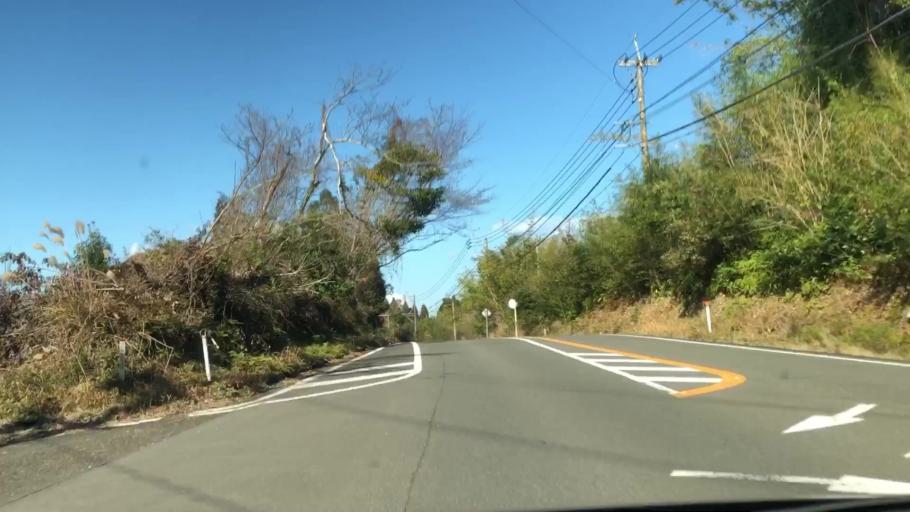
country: JP
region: Kagoshima
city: Satsumasendai
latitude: 31.8537
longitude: 130.4293
